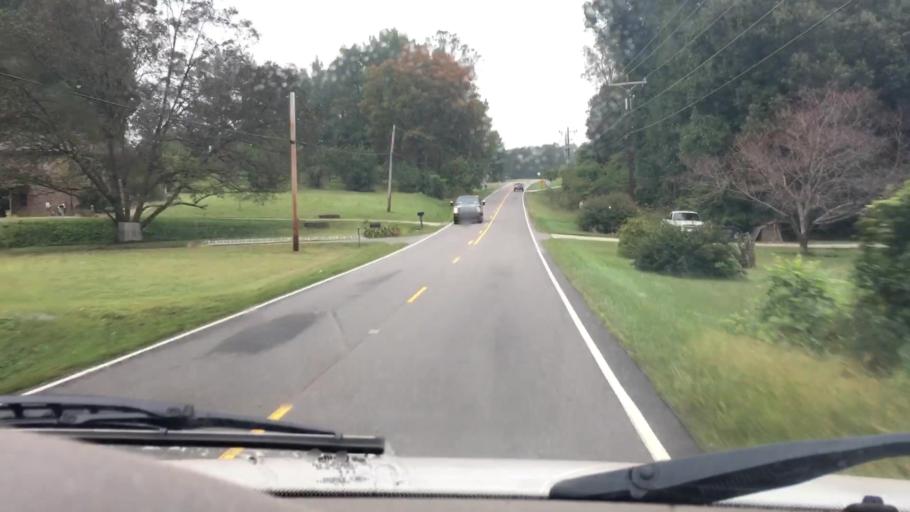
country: US
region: North Carolina
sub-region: Iredell County
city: Mooresville
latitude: 35.6348
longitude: -80.7767
